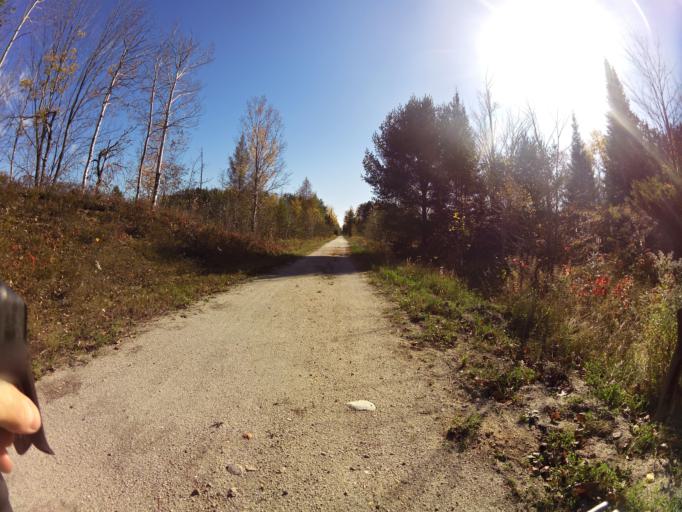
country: CA
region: Quebec
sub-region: Outaouais
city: Wakefield
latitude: 45.9075
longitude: -76.0411
